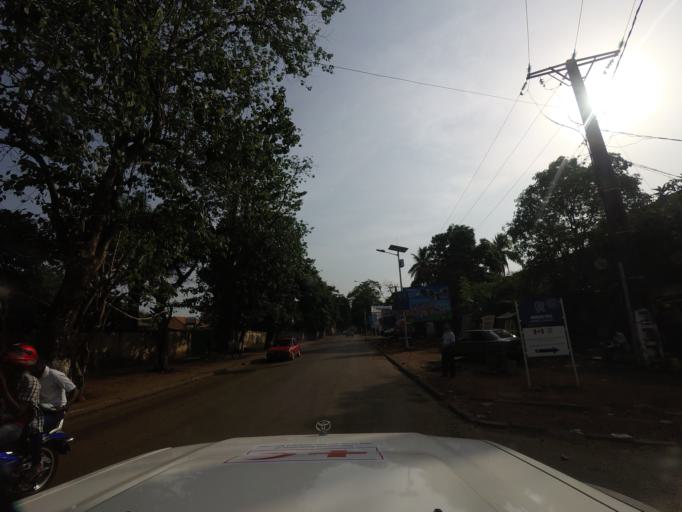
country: GN
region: Conakry
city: Conakry
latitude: 9.5397
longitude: -13.6821
